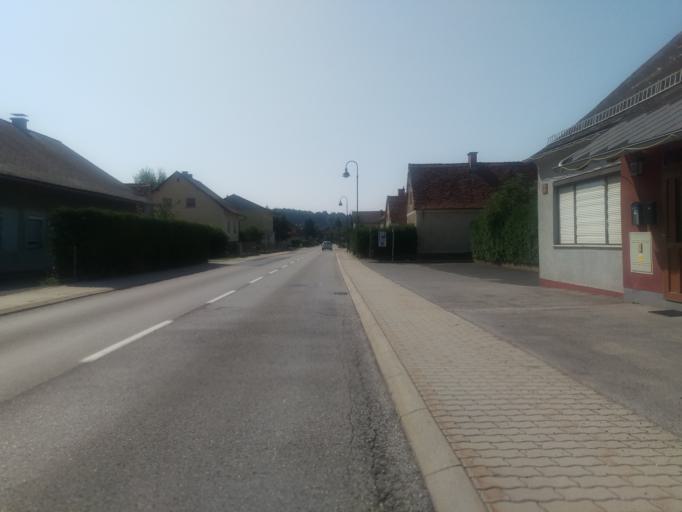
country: AT
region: Styria
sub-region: Politischer Bezirk Graz-Umgebung
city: Fernitz
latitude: 46.9700
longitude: 15.5006
